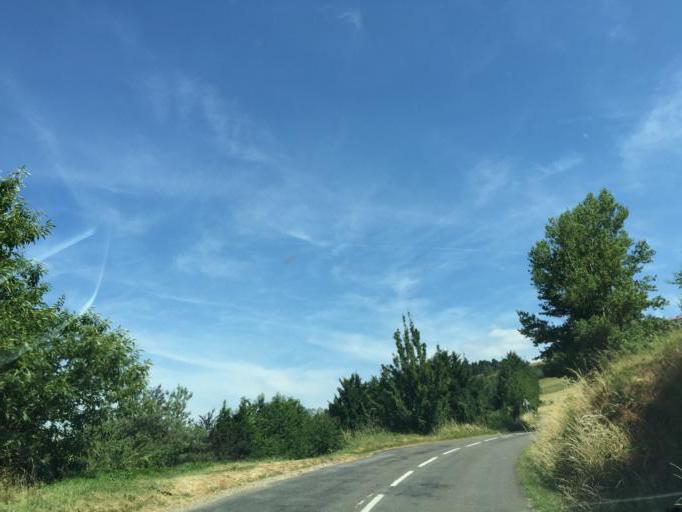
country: FR
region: Rhone-Alpes
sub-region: Departement de la Loire
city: Saint-Chamond
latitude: 45.4096
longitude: 4.5208
